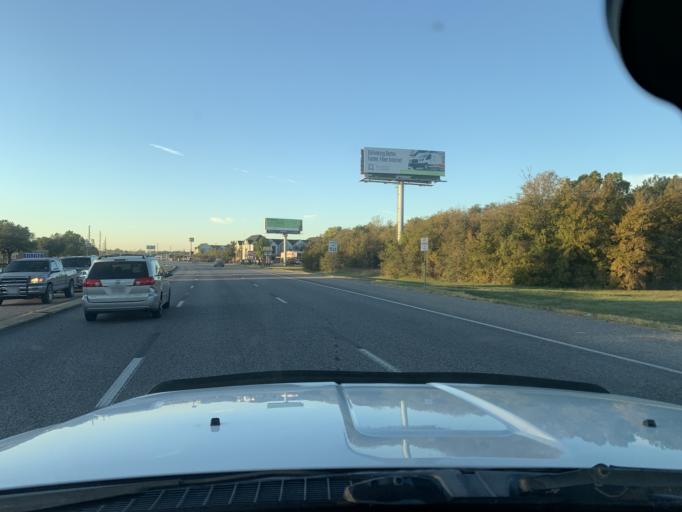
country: US
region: Texas
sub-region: Fort Bend County
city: Four Corners
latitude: 29.6496
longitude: -95.6510
